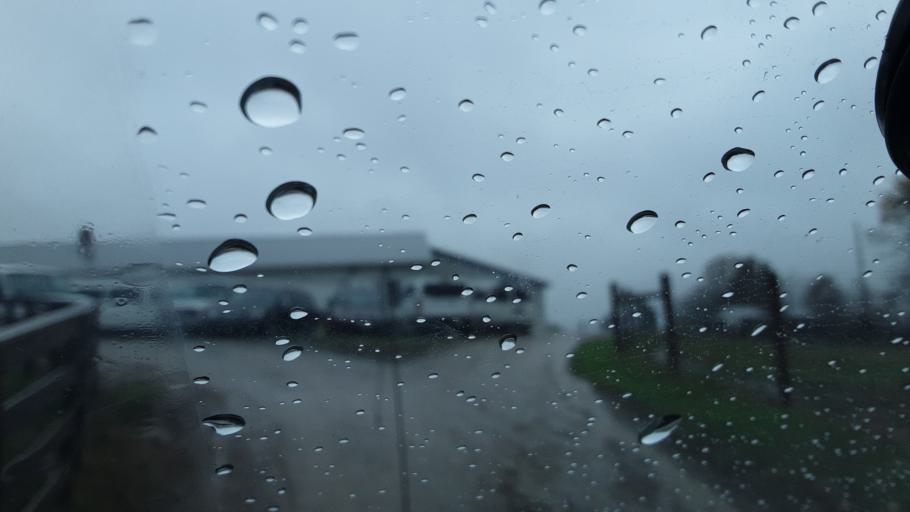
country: US
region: Ohio
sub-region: Vinton County
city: McArthur
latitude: 39.2246
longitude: -82.4608
